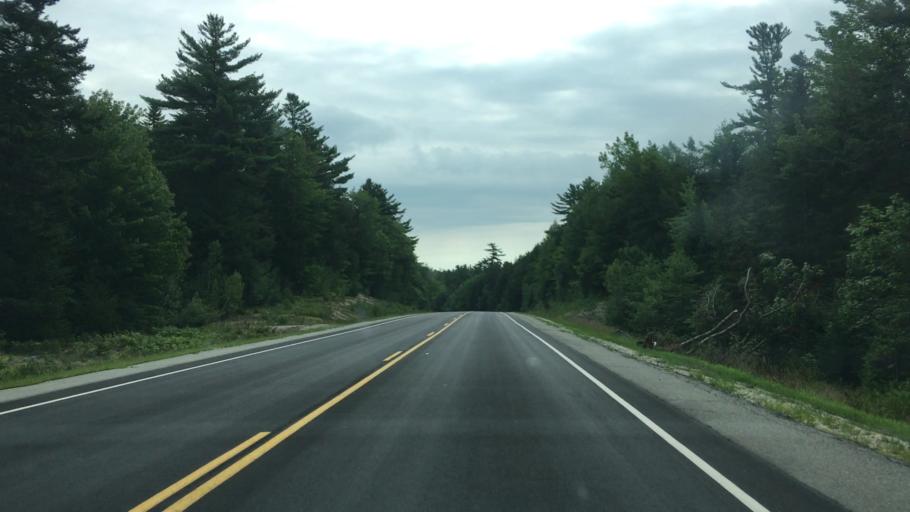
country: US
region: Maine
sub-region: Washington County
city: Addison
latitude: 44.9091
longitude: -67.8460
